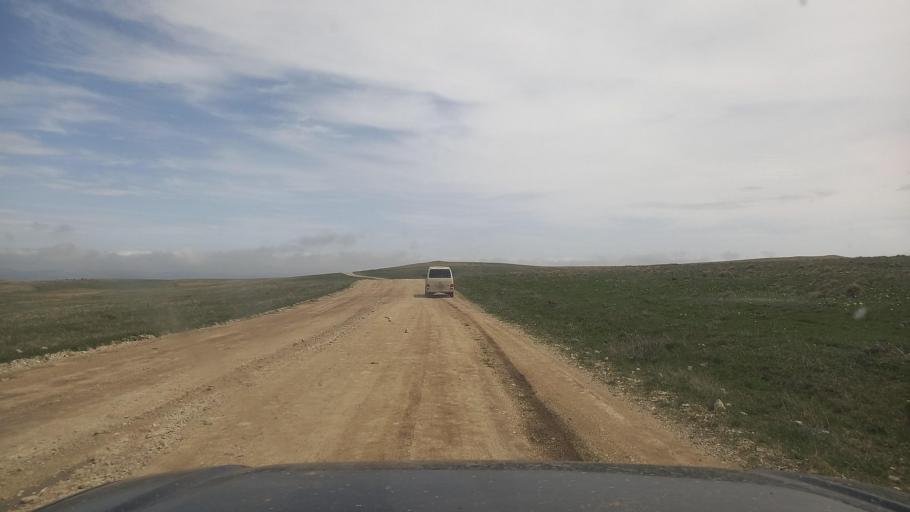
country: RU
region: Stavropol'skiy
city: Kislovodsk
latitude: 43.7614
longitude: 42.8027
